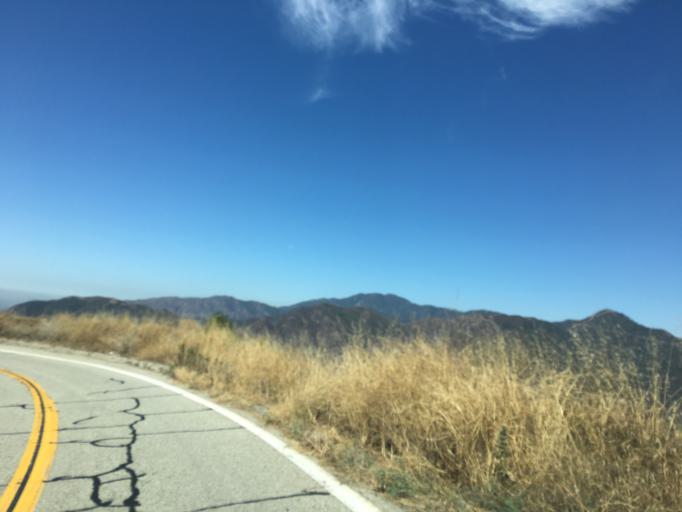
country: US
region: California
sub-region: Los Angeles County
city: Glendora
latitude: 34.1943
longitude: -117.8410
